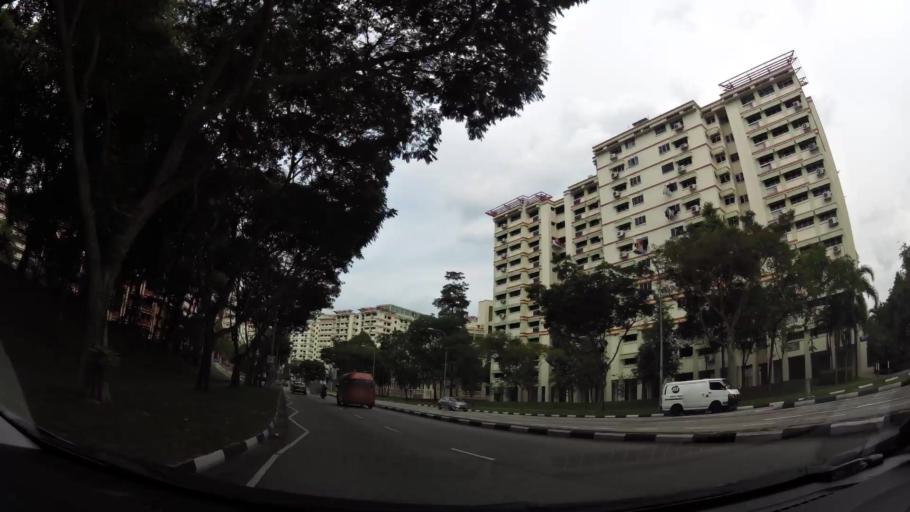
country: MY
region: Johor
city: Johor Bahru
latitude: 1.4341
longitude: 103.7950
